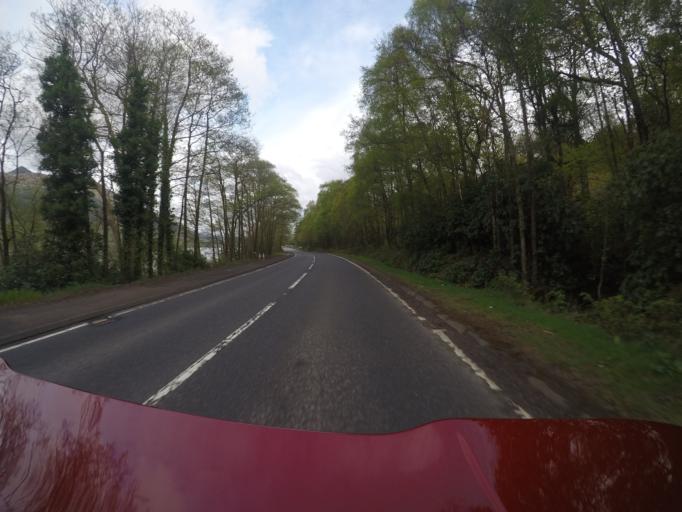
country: GB
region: Scotland
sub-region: Argyll and Bute
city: Garelochhead
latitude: 56.1960
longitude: -4.7033
